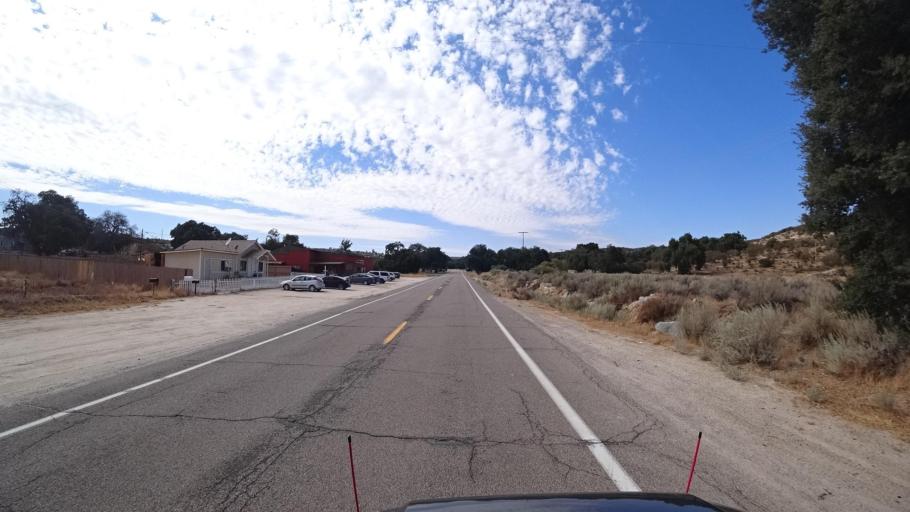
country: MX
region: Baja California
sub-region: Tecate
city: Cereso del Hongo
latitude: 32.6640
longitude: -116.2745
